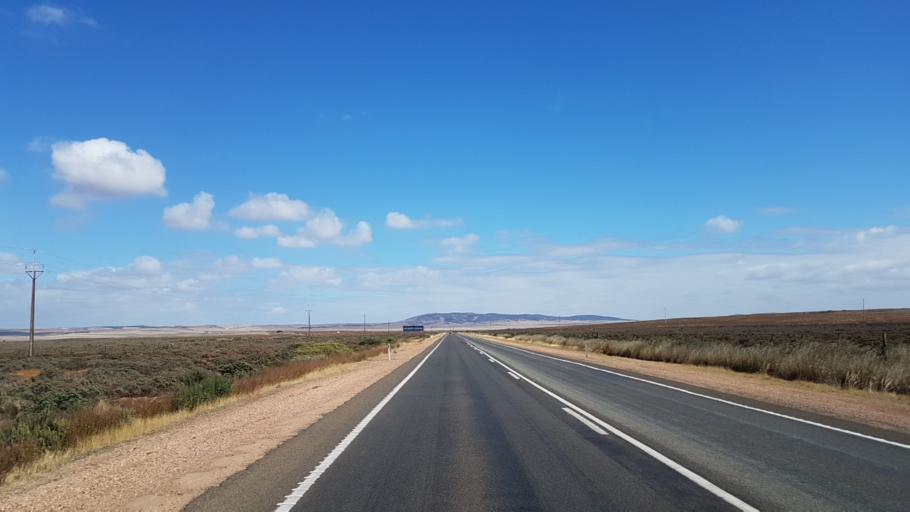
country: AU
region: South Australia
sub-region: Wakefield
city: Balaklava
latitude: -34.1307
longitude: 138.1416
